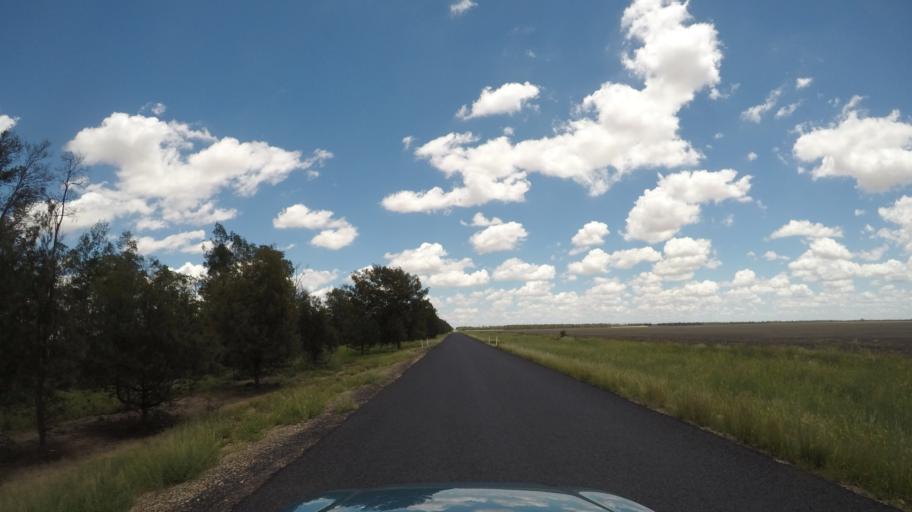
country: AU
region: Queensland
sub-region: Goondiwindi
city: Goondiwindi
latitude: -28.1712
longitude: 150.2206
